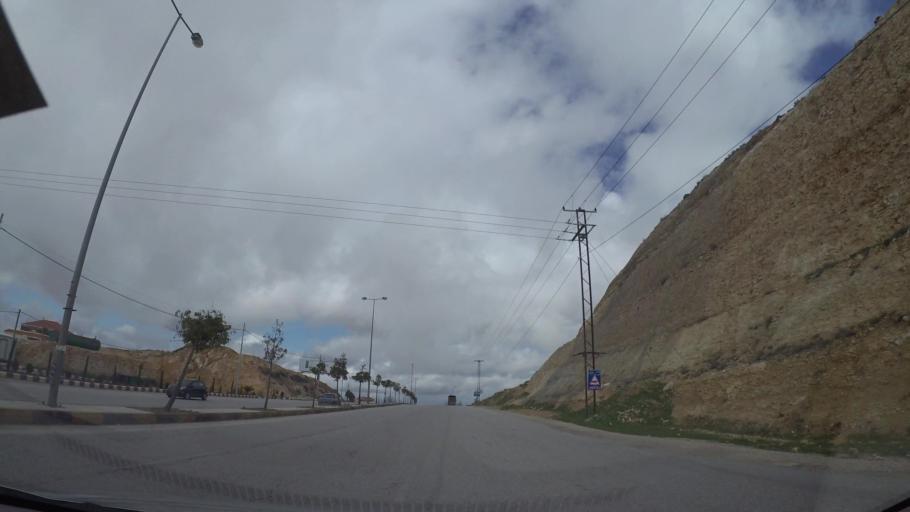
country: JO
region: Amman
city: Al Jubayhah
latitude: 32.0515
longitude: 35.8711
